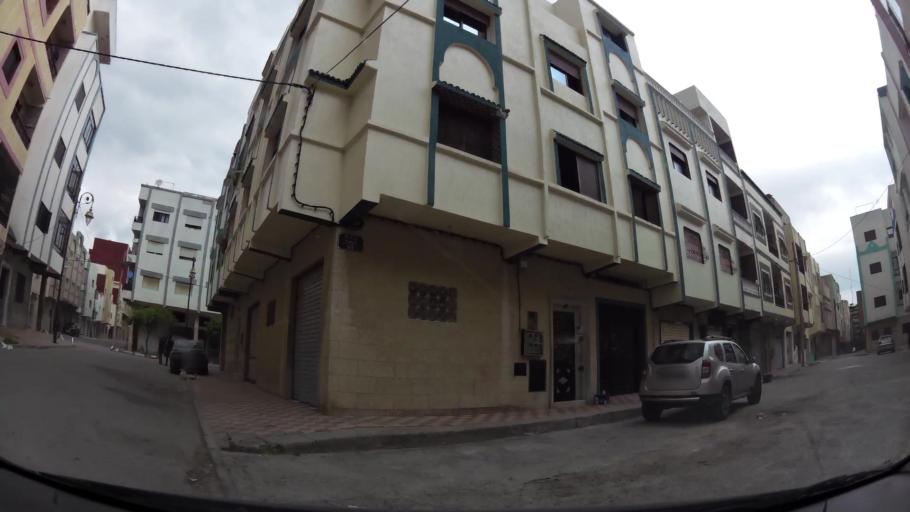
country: MA
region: Tanger-Tetouan
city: Tetouan
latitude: 35.5637
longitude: -5.3615
